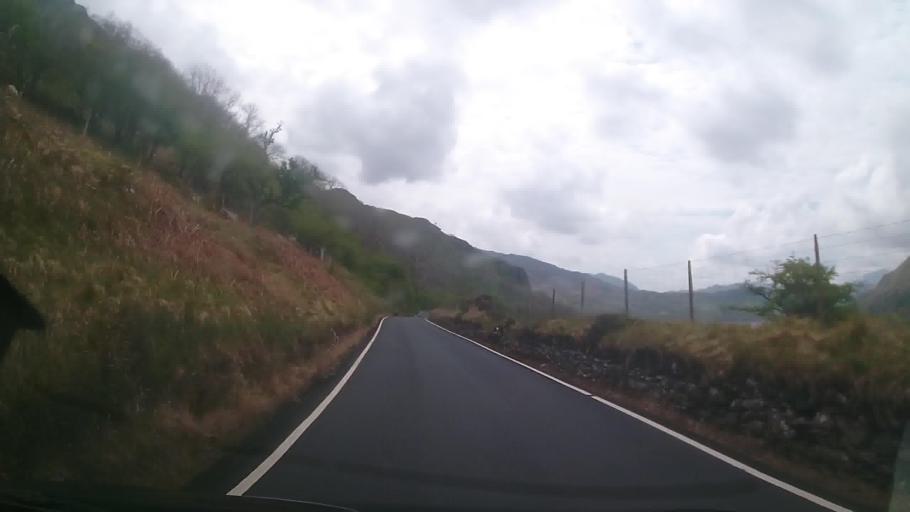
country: GB
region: Wales
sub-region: Gwynedd
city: Blaenau-Ffestiniog
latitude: 53.0642
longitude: -4.0016
